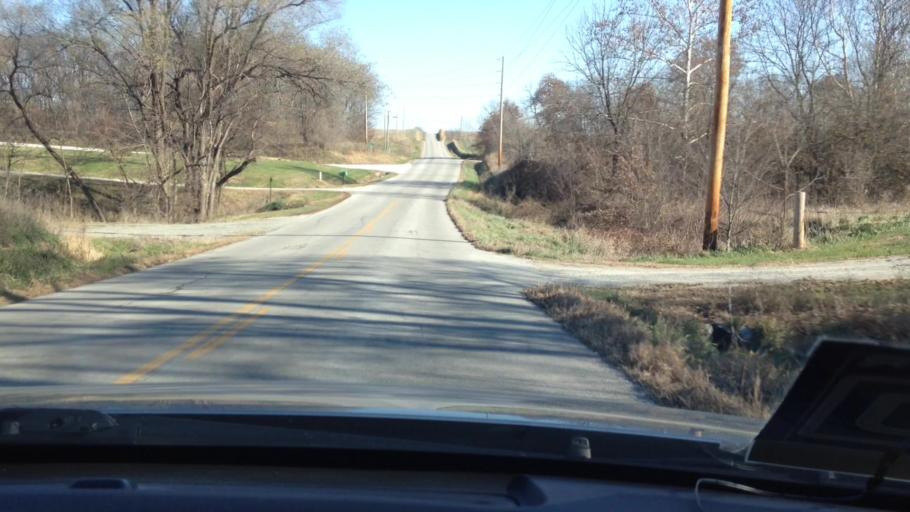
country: US
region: Missouri
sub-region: Platte County
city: Weston
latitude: 39.4982
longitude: -94.8186
